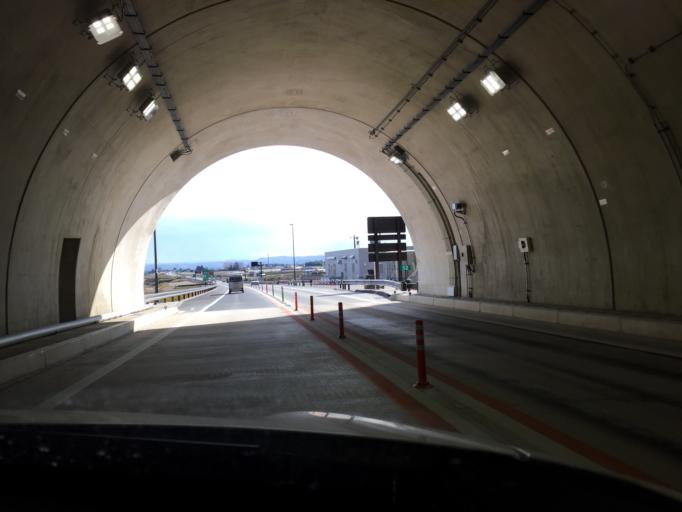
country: JP
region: Fukushima
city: Fukushima-shi
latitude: 37.8269
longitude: 140.4007
